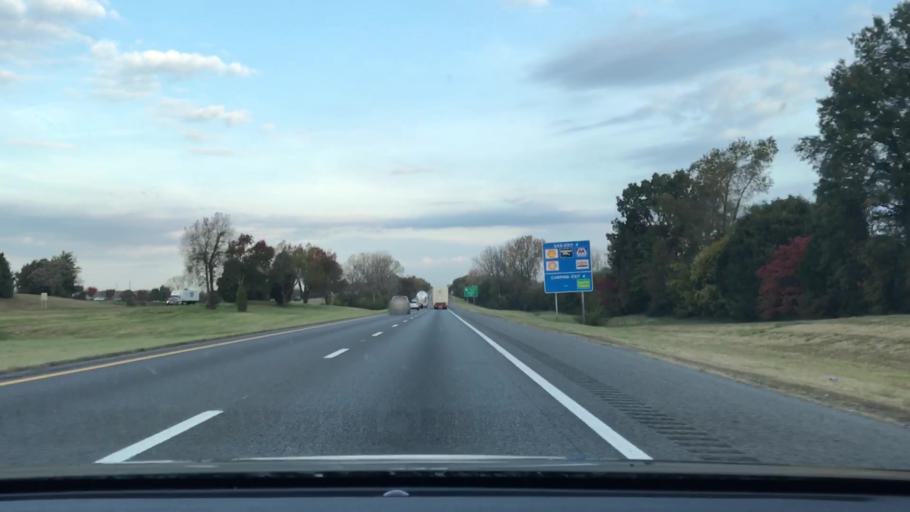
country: US
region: Tennessee
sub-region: Montgomery County
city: Clarksville
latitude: 36.5817
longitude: -87.2661
